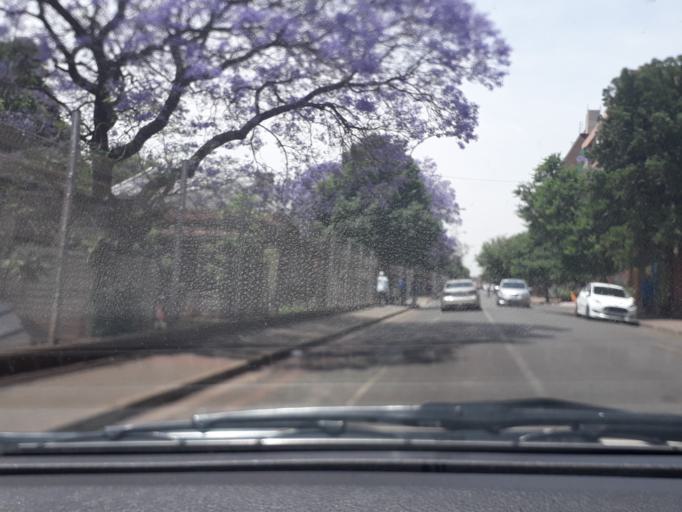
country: ZA
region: Gauteng
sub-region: City of Johannesburg Metropolitan Municipality
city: Johannesburg
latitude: -26.1859
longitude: 28.0515
